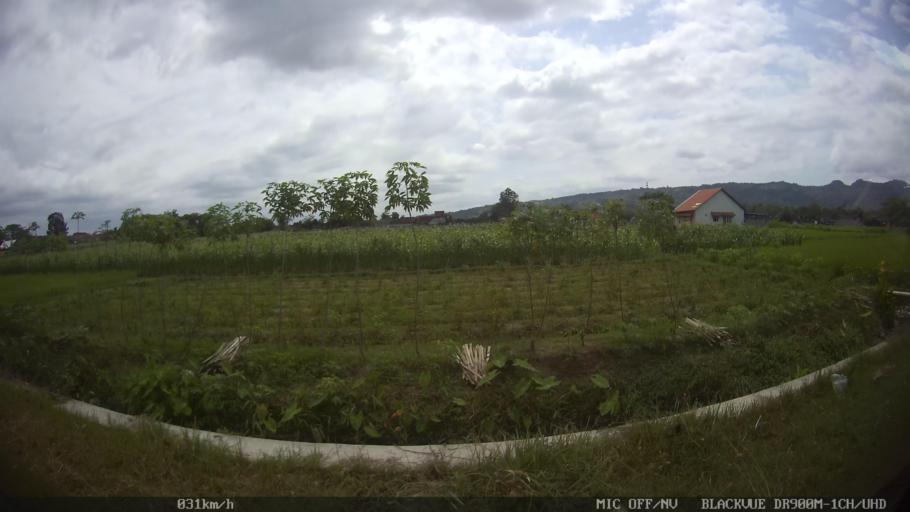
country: ID
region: Central Java
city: Candi Prambanan
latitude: -7.8125
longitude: 110.4930
